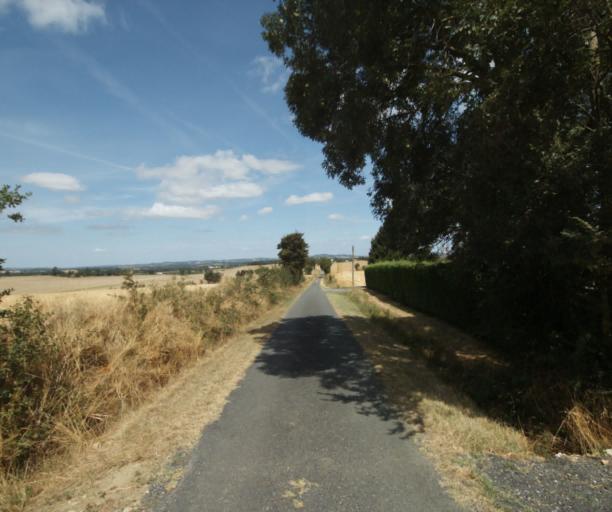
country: FR
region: Midi-Pyrenees
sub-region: Departement du Tarn
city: Dourgne
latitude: 43.4902
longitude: 2.1056
